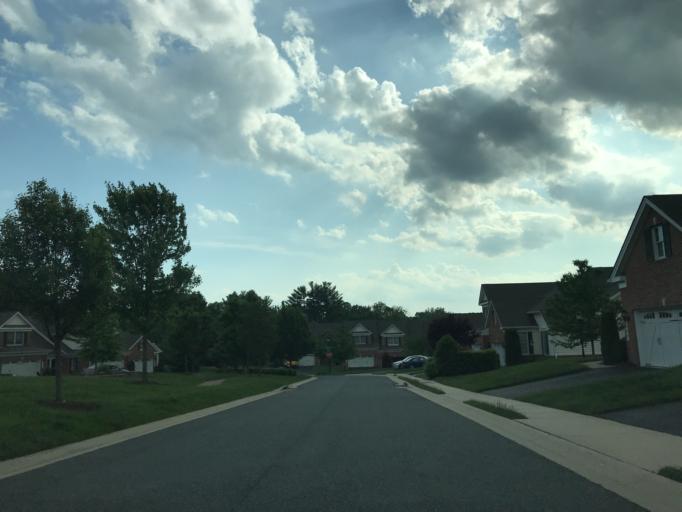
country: US
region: Maryland
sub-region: Harford County
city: North Bel Air
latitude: 39.5212
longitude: -76.3663
